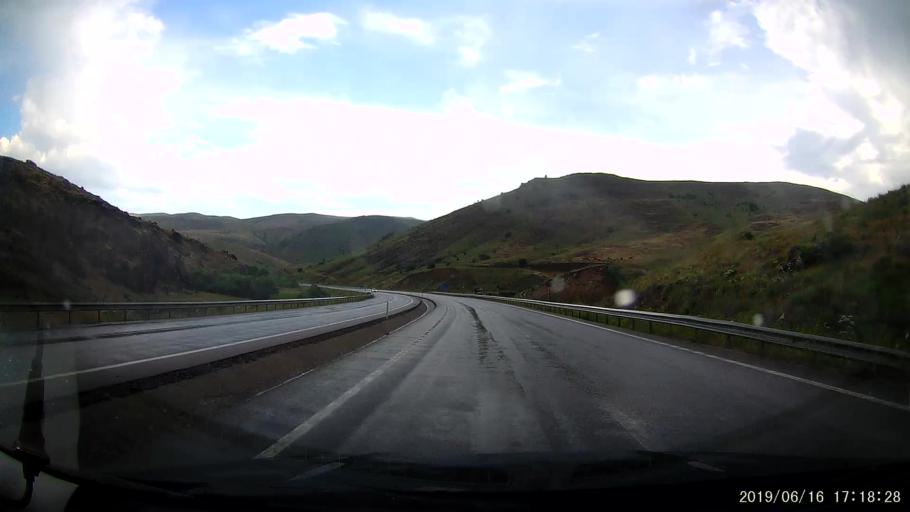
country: TR
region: Erzincan
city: Tercan
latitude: 39.8138
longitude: 40.5287
